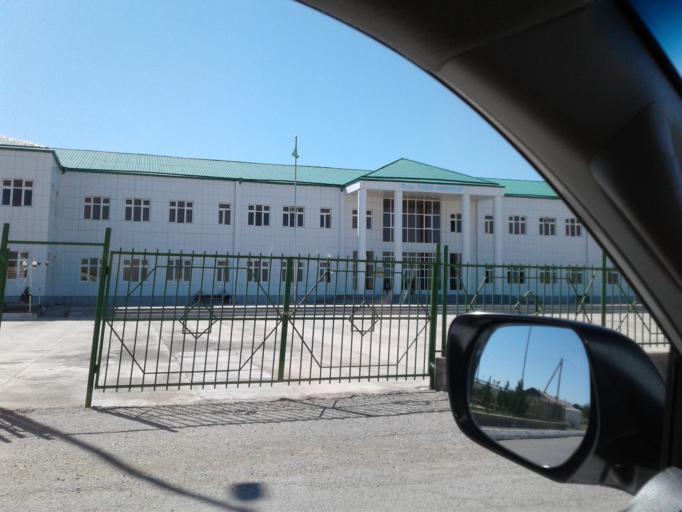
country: TM
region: Mary
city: Bayramaly
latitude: 38.0889
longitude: 62.7959
